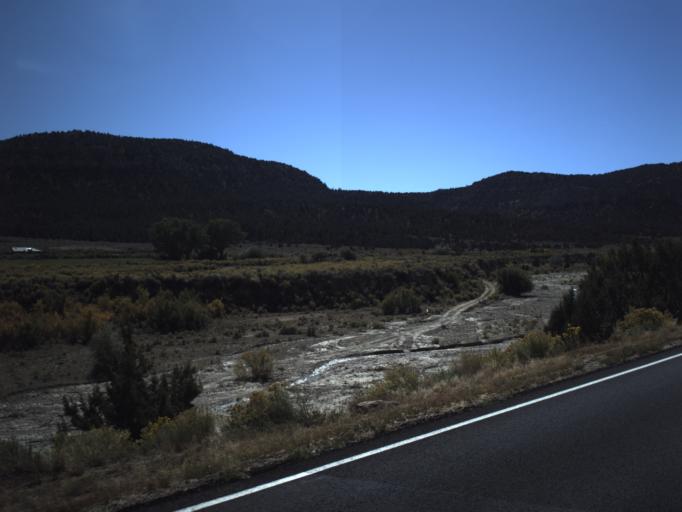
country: US
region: Utah
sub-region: Wayne County
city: Loa
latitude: 37.7338
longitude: -111.7529
